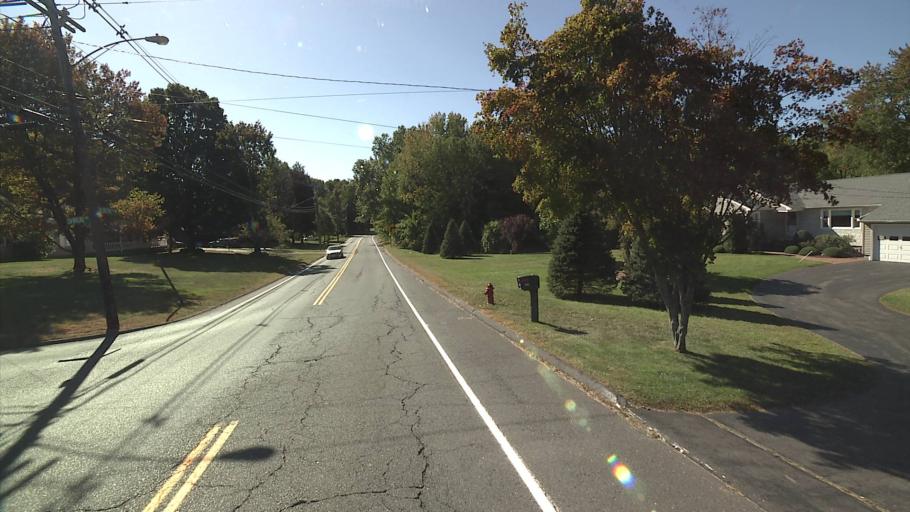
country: US
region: Connecticut
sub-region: Hartford County
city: Bristol
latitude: 41.7132
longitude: -72.9458
